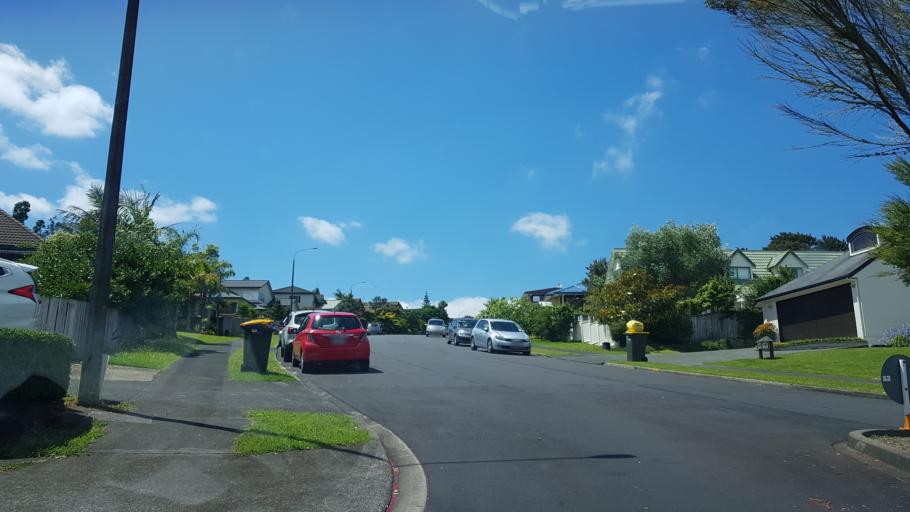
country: NZ
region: Auckland
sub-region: Auckland
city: North Shore
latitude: -36.7858
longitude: 174.7074
